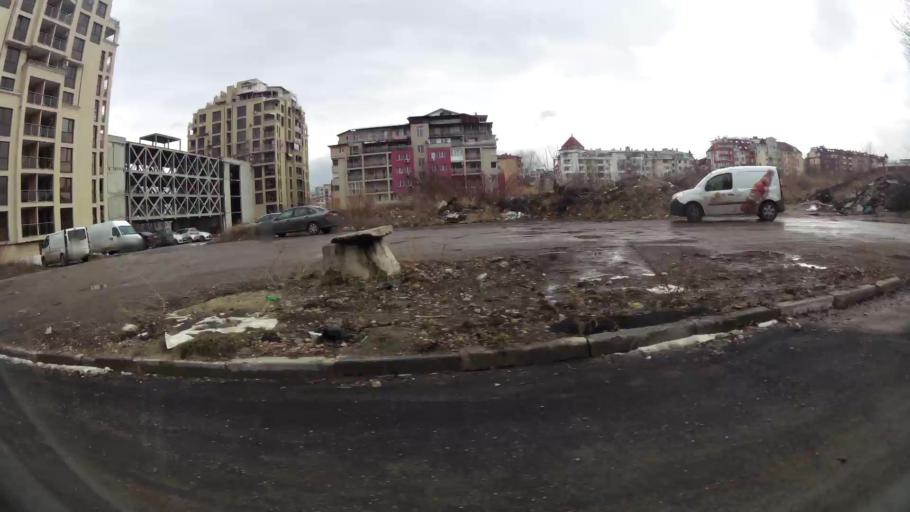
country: BG
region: Sofiya
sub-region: Obshtina Bozhurishte
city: Bozhurishte
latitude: 42.7237
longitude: 23.2568
